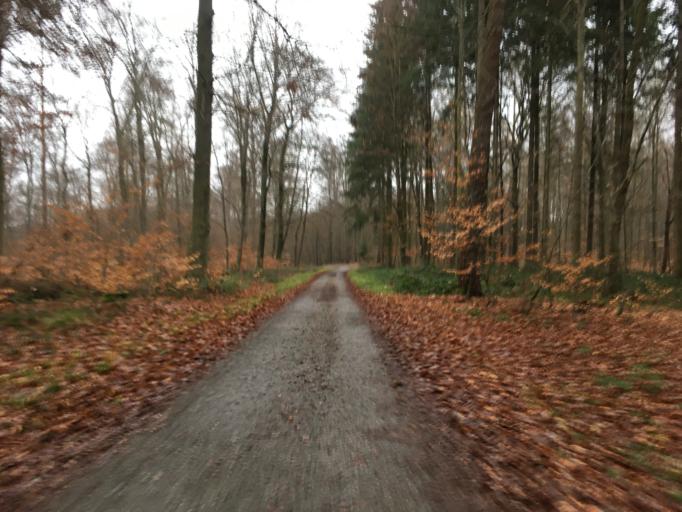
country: DE
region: Baden-Wuerttemberg
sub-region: Karlsruhe Region
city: Konigsbach-Stein
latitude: 48.9537
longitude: 8.5263
